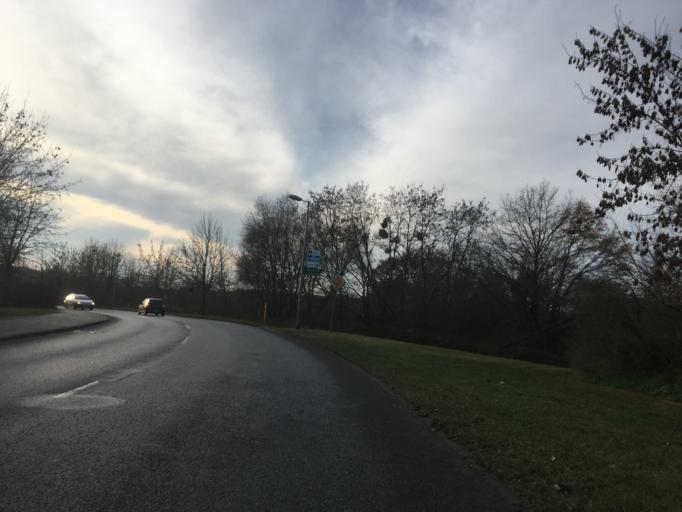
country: DE
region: Brandenburg
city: Eberswalde
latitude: 52.8408
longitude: 13.8103
